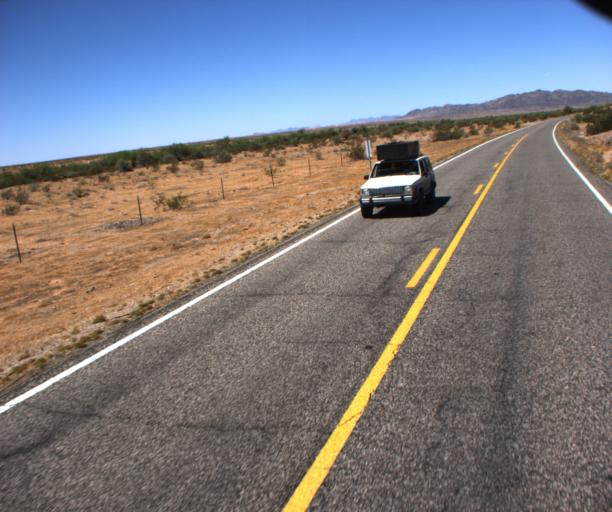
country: US
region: Arizona
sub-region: La Paz County
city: Parker
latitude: 33.9946
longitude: -114.1668
